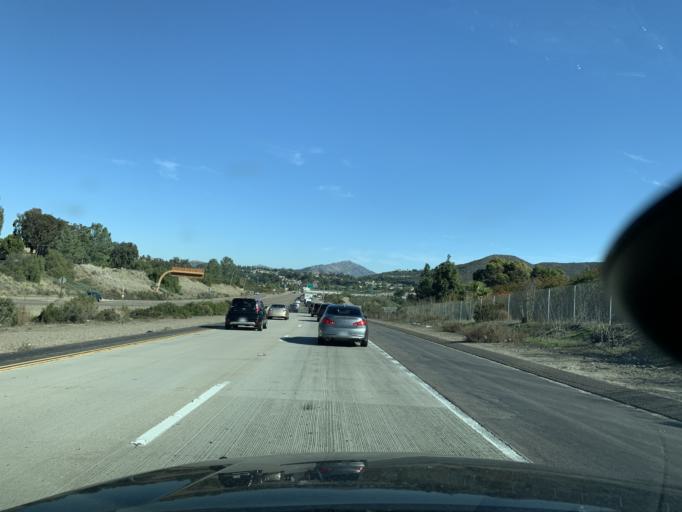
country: US
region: California
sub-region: San Diego County
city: Poway
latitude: 32.9624
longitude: -117.1016
